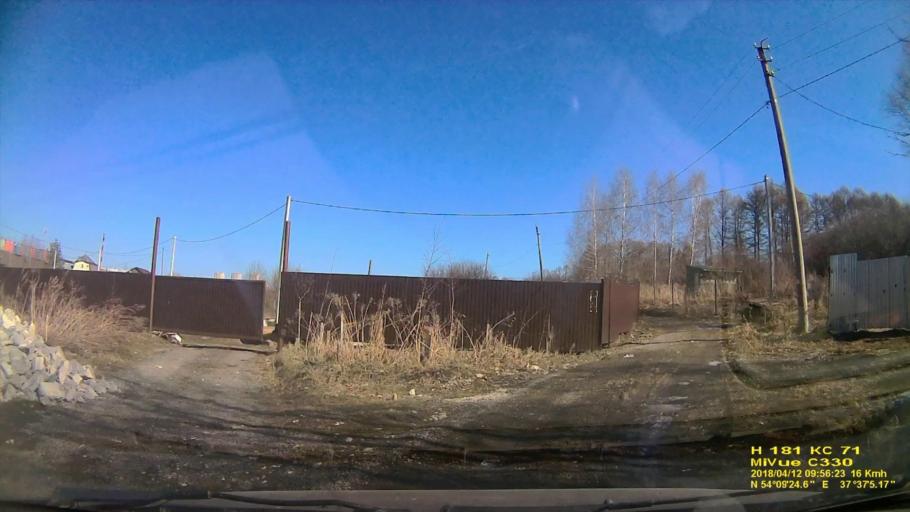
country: RU
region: Tula
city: Mendeleyevskiy
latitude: 54.1569
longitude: 37.6182
